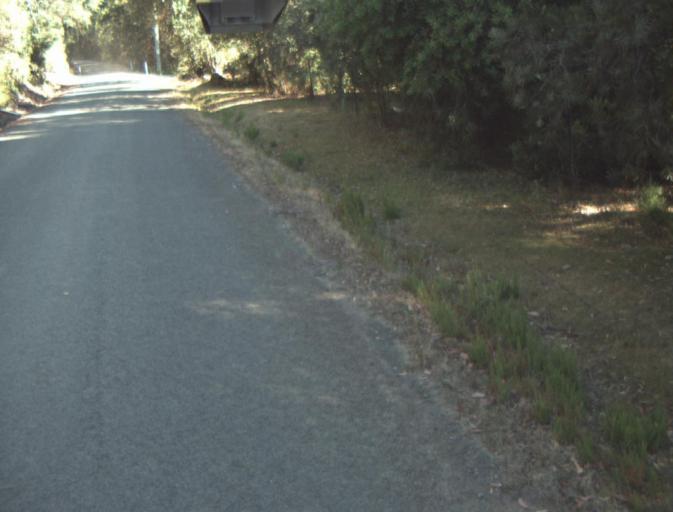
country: AU
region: Tasmania
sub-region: Launceston
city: Mayfield
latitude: -41.3035
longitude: 147.1924
